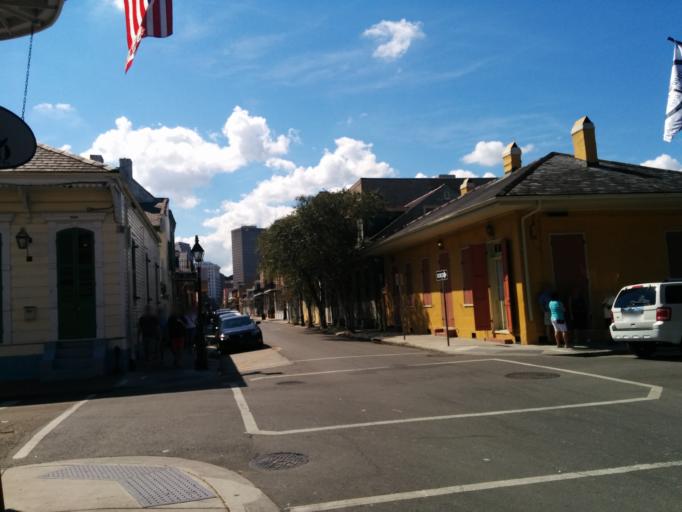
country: US
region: Louisiana
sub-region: Orleans Parish
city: New Orleans
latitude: 29.9598
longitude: -90.0673
